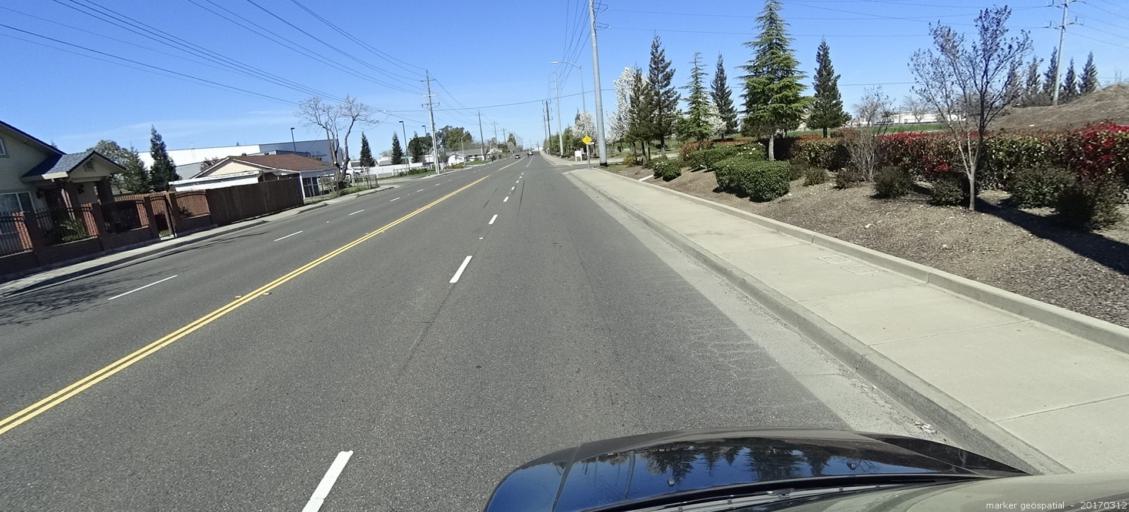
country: US
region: California
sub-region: Sacramento County
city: Arden-Arcade
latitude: 38.6410
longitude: -121.4106
